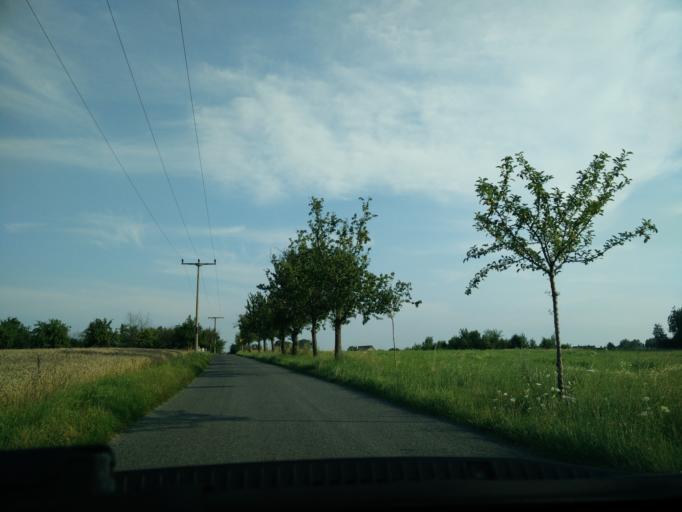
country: DE
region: Saxony
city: Frohburg
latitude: 51.0908
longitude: 12.5599
